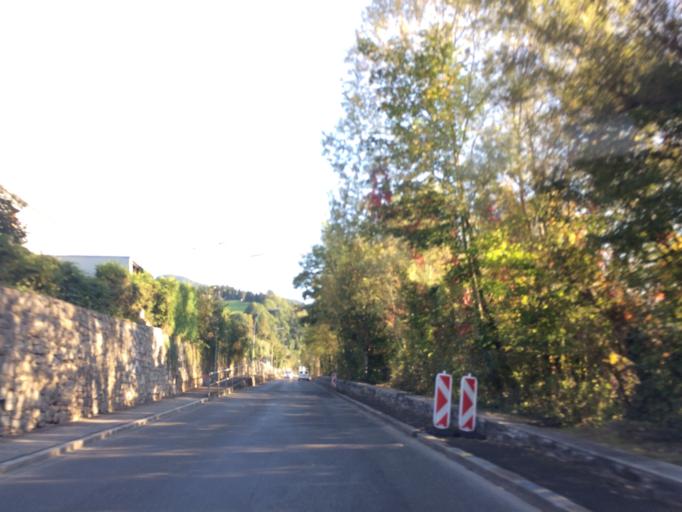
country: AT
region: Styria
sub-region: Politischer Bezirk Leoben
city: Leoben
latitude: 47.3743
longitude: 15.0957
